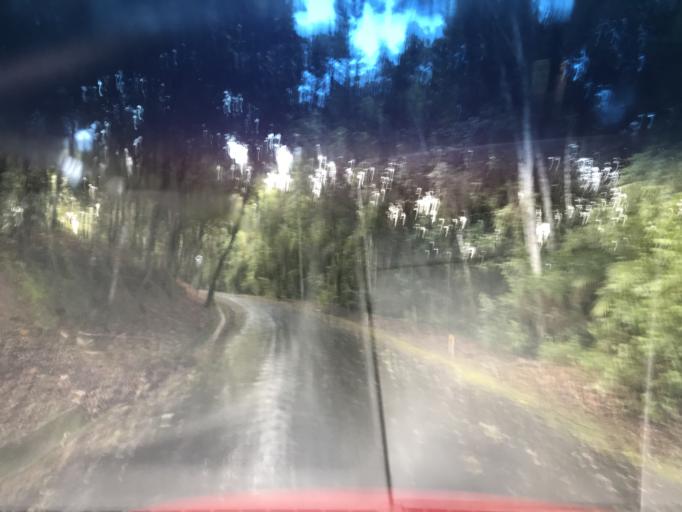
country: BR
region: Bahia
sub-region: Gandu
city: Gandu
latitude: -13.9013
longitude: -39.4601
